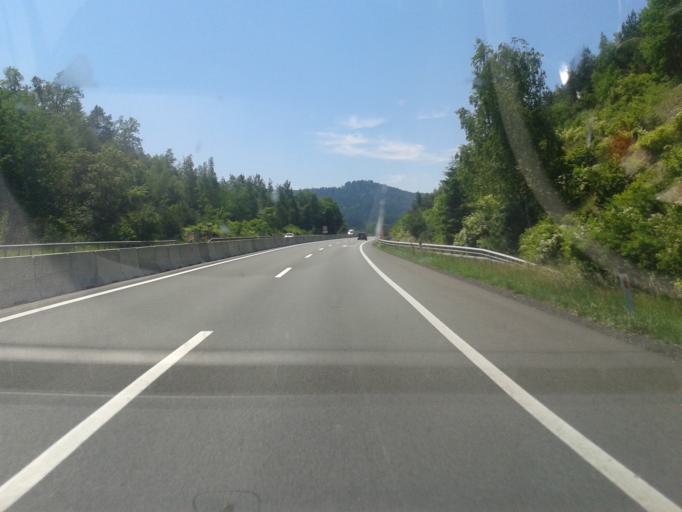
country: AT
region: Carinthia
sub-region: Politischer Bezirk Wolfsberg
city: Sankt Andrae
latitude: 46.7500
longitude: 14.8145
